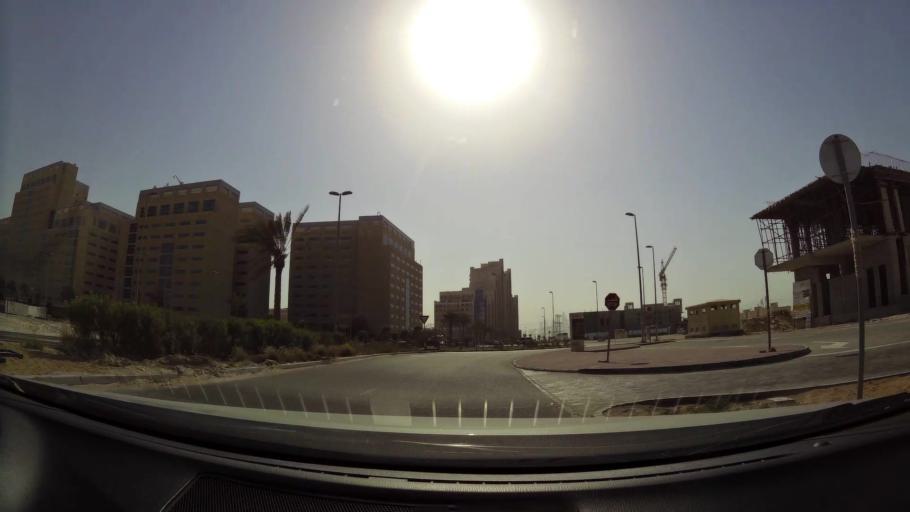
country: AE
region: Dubai
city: Dubai
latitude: 25.0682
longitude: 55.2111
